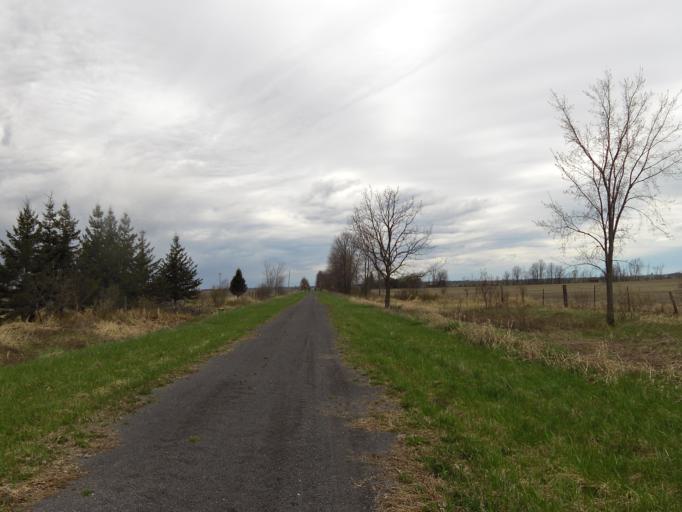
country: CA
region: Ontario
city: Hawkesbury
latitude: 45.5431
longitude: -74.8136
